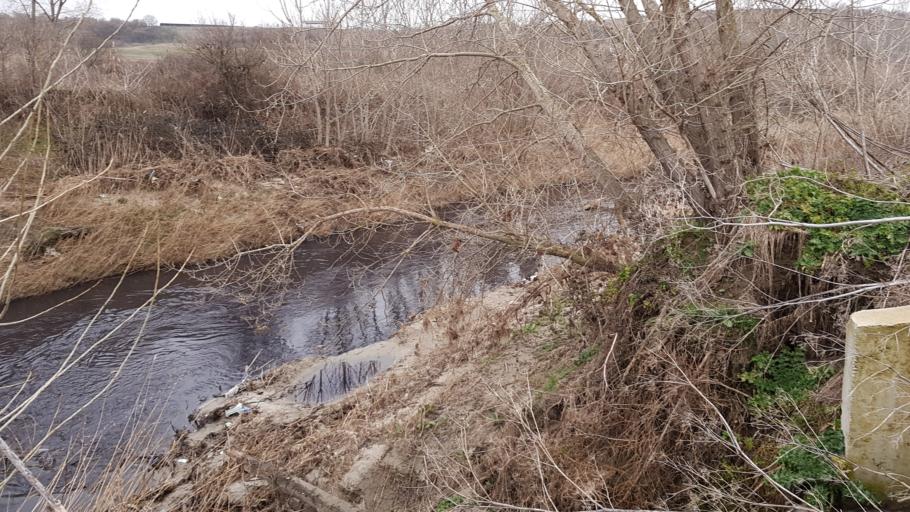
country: TR
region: Tekirdag
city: Muratli
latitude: 41.1784
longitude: 27.4766
